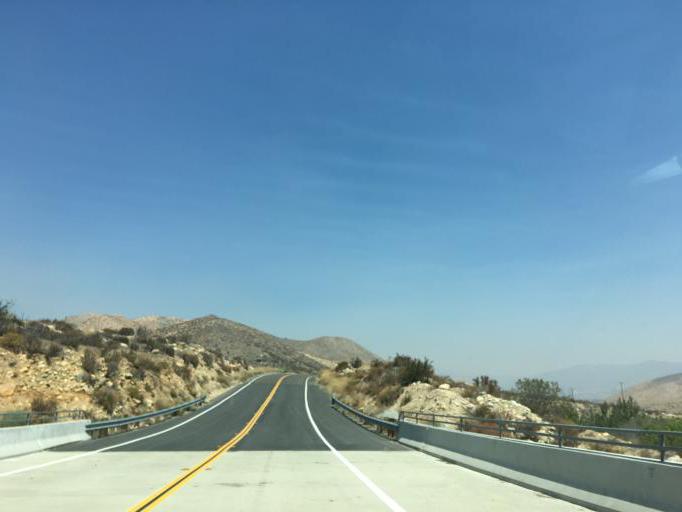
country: US
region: California
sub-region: Los Angeles County
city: Acton
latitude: 34.4432
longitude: -118.1500
